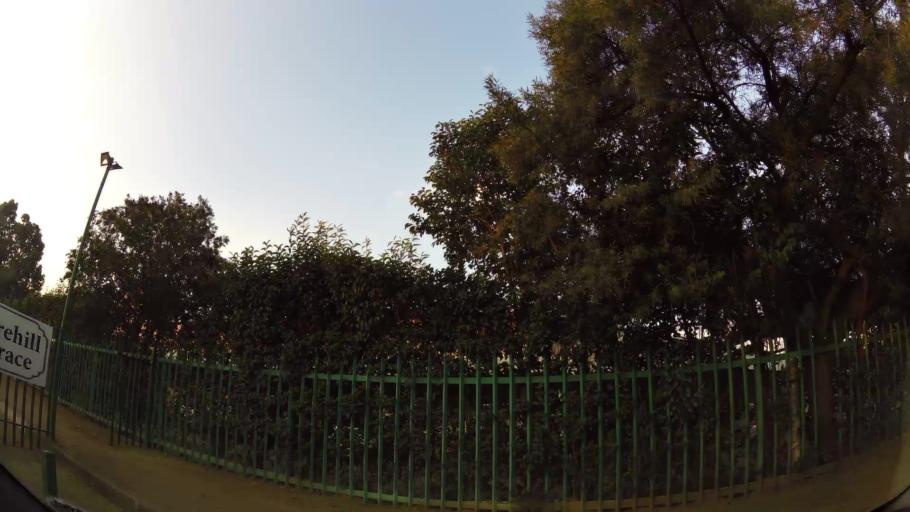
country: ZA
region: Gauteng
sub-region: Ekurhuleni Metropolitan Municipality
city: Benoni
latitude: -26.1727
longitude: 28.3379
